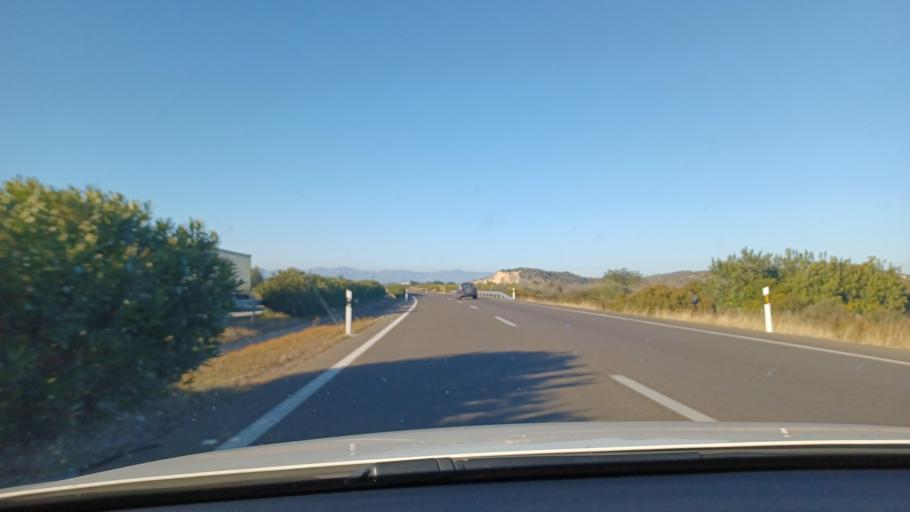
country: ES
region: Valencia
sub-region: Provincia de Castello
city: Vinaros
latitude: 40.4795
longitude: 0.4188
